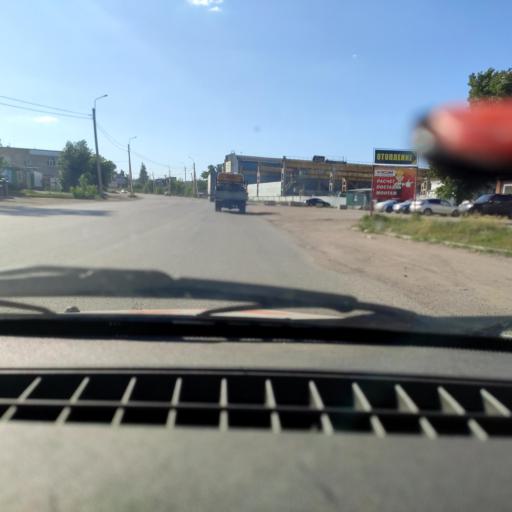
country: RU
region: Bashkortostan
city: Sterlitamak
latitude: 53.6519
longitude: 55.9748
